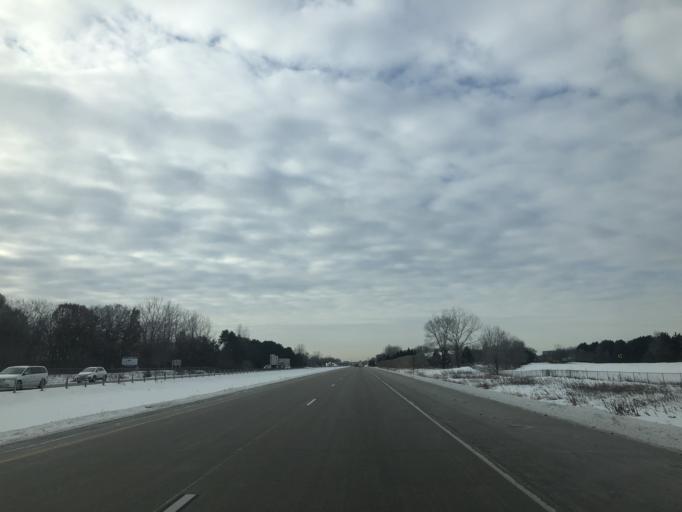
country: US
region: Minnesota
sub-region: Anoka County
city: Circle Pines
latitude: 45.1712
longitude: -93.1309
